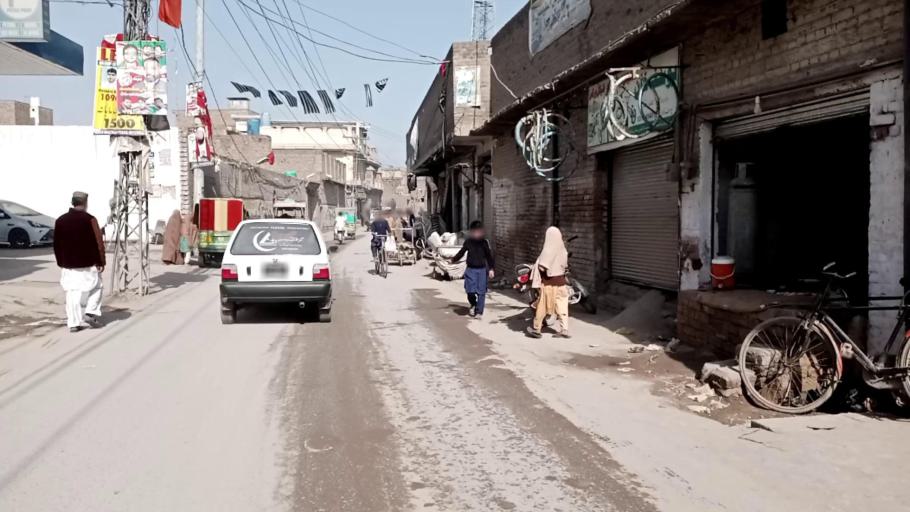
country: PK
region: Khyber Pakhtunkhwa
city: Peshawar
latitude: 33.9915
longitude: 71.5803
